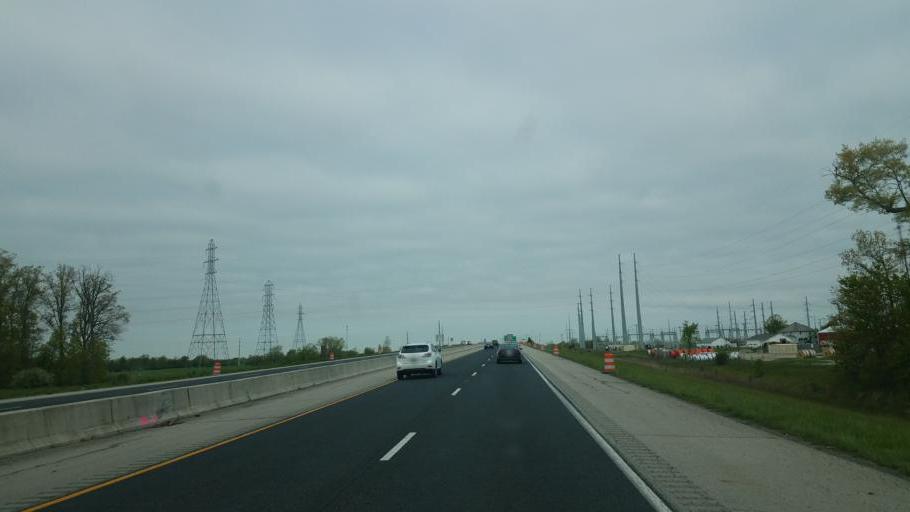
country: US
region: Indiana
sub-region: Allen County
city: Fort Wayne
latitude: 41.1680
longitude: -85.0888
